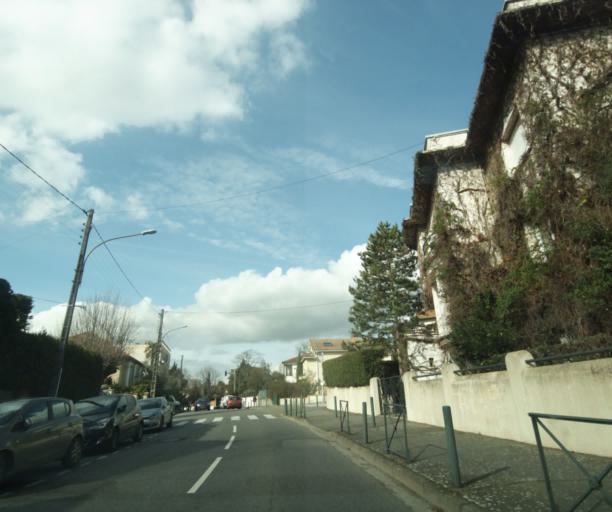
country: FR
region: Midi-Pyrenees
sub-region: Departement de la Haute-Garonne
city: Toulouse
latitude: 43.5999
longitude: 1.4724
